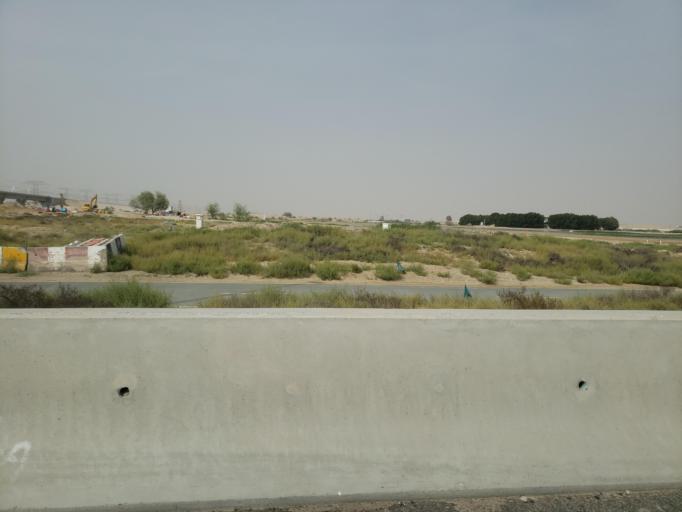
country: AE
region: Dubai
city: Dubai
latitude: 25.0191
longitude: 55.2849
